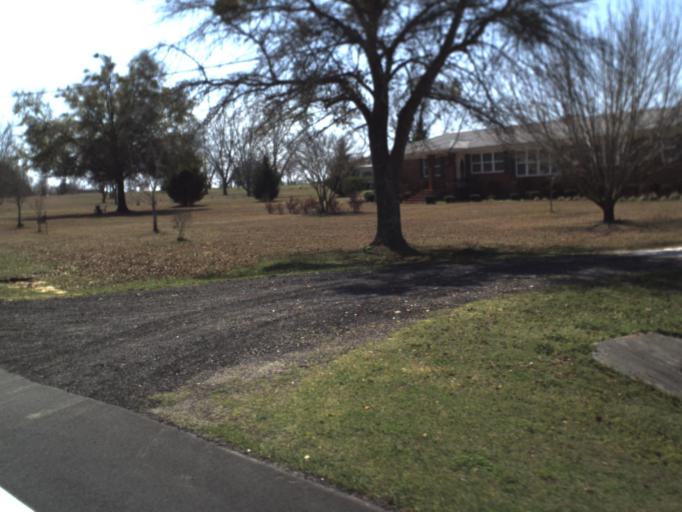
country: US
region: Florida
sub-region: Jackson County
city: Sneads
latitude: 30.7851
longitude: -85.0190
